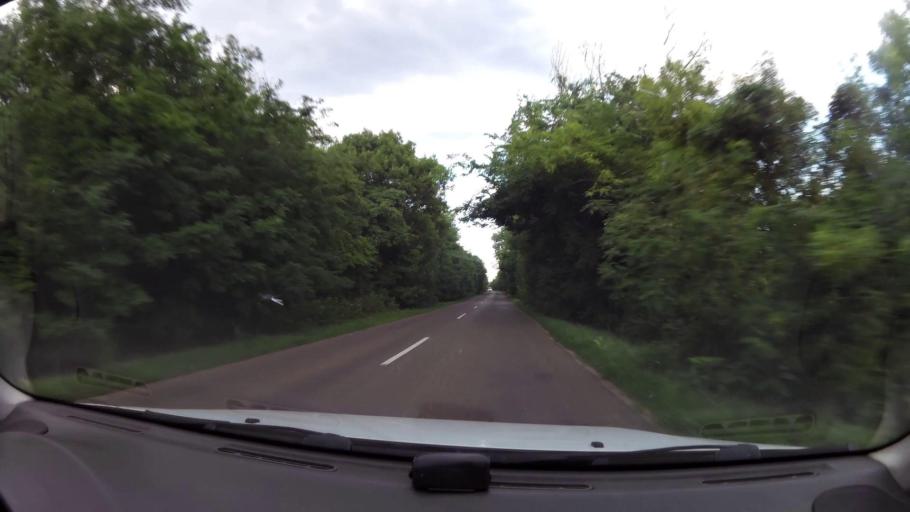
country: HU
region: Pest
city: Tapiosag
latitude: 47.3929
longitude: 19.6400
